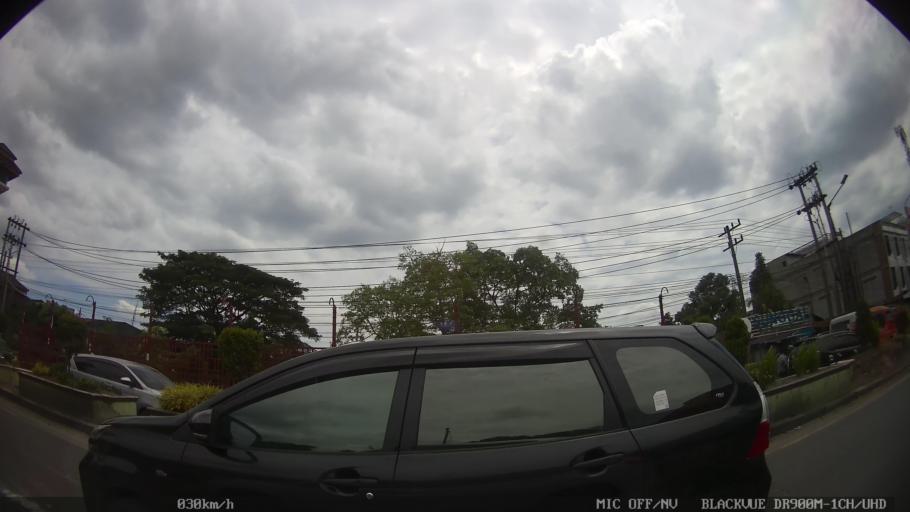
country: ID
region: North Sumatra
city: Sunggal
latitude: 3.5988
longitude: 98.6053
